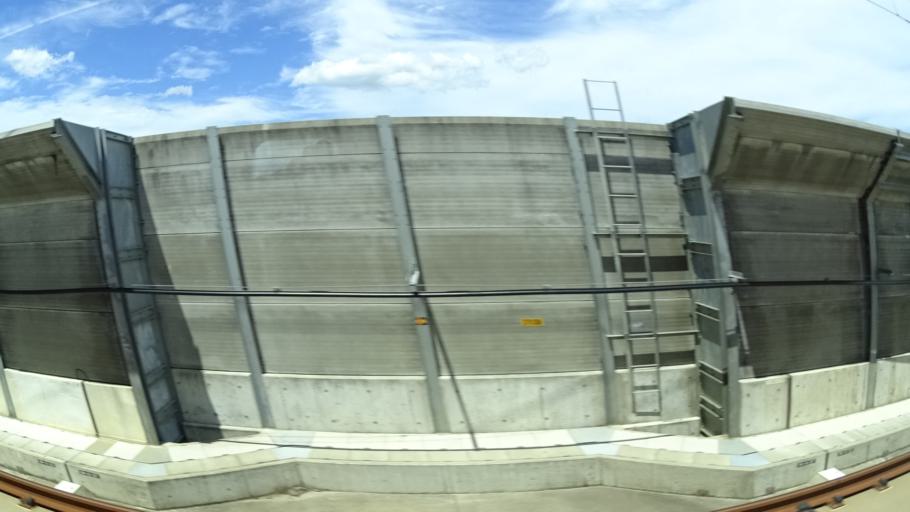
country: JP
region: Toyama
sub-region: Oyabe Shi
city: Oyabe
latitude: 36.6725
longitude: 136.8951
